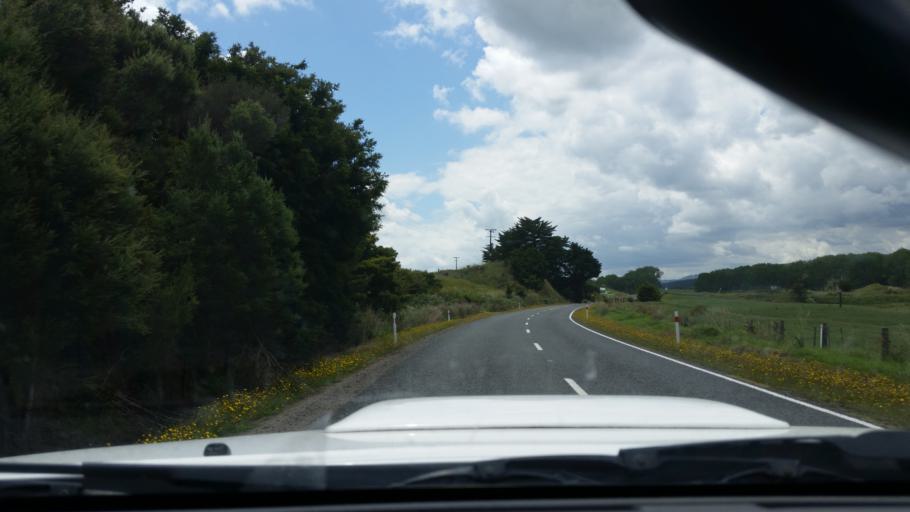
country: NZ
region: Northland
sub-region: Kaipara District
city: Dargaville
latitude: -35.8577
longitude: 173.8468
